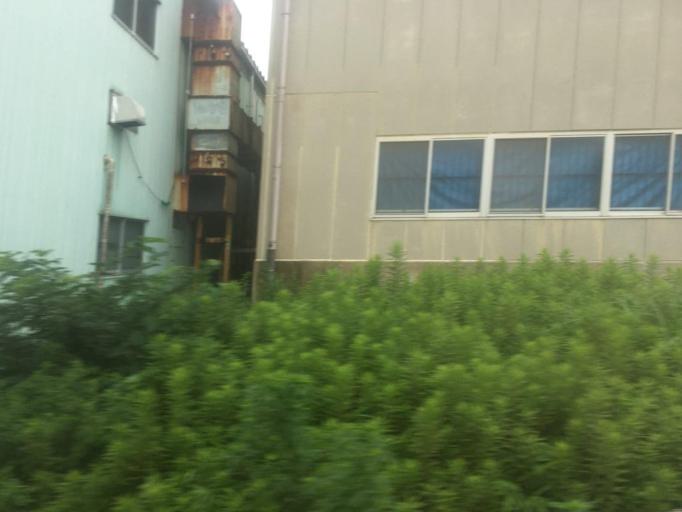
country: JP
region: Chiba
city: Yotsukaido
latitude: 35.7166
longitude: 140.1372
